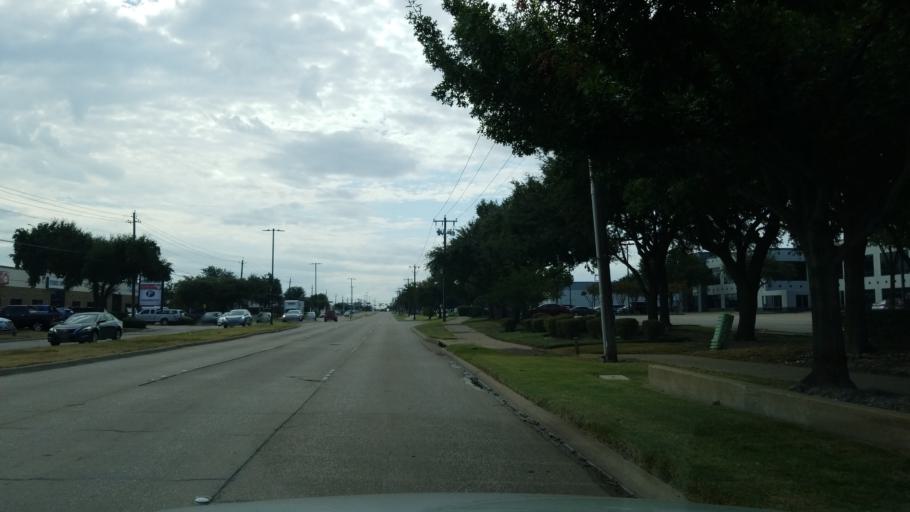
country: US
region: Texas
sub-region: Dallas County
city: Garland
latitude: 32.8927
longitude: -96.6831
